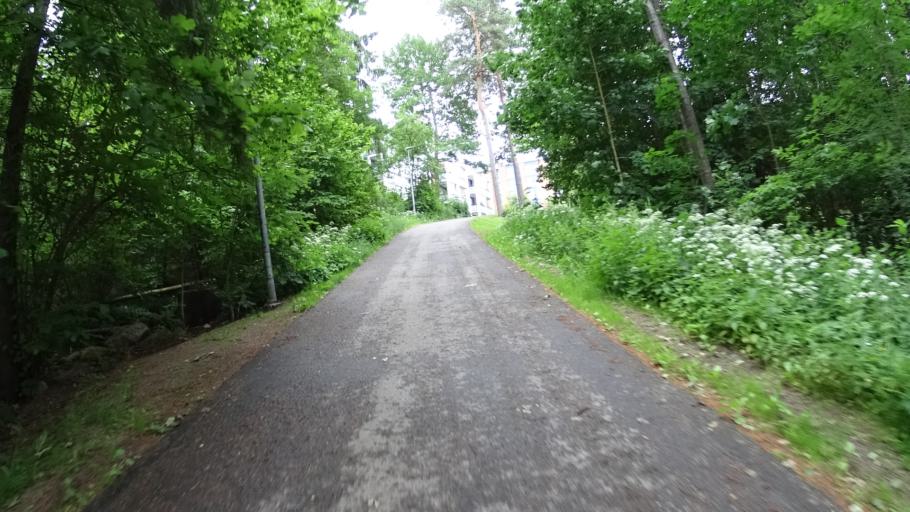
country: FI
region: Uusimaa
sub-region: Helsinki
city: Kilo
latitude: 60.2654
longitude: 24.8014
